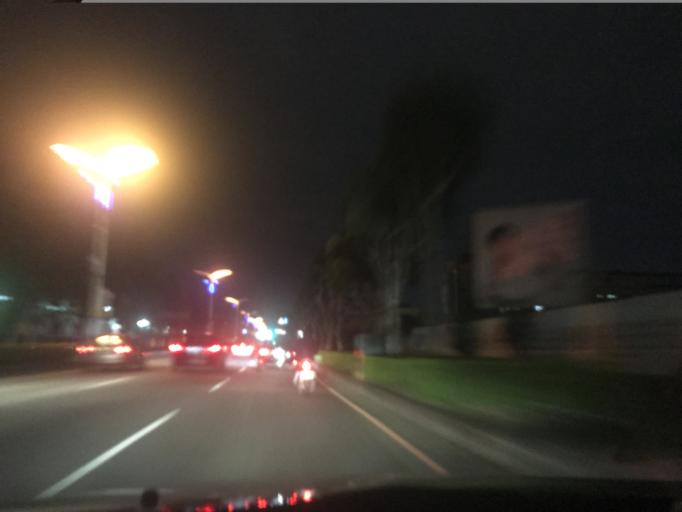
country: TW
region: Taiwan
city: Taoyuan City
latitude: 24.9804
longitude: 121.2362
